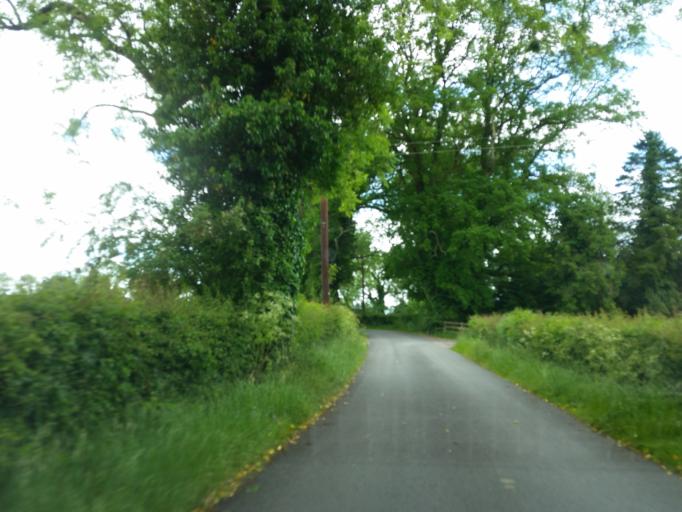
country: GB
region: Northern Ireland
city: Fivemiletown
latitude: 54.3883
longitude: -7.2344
